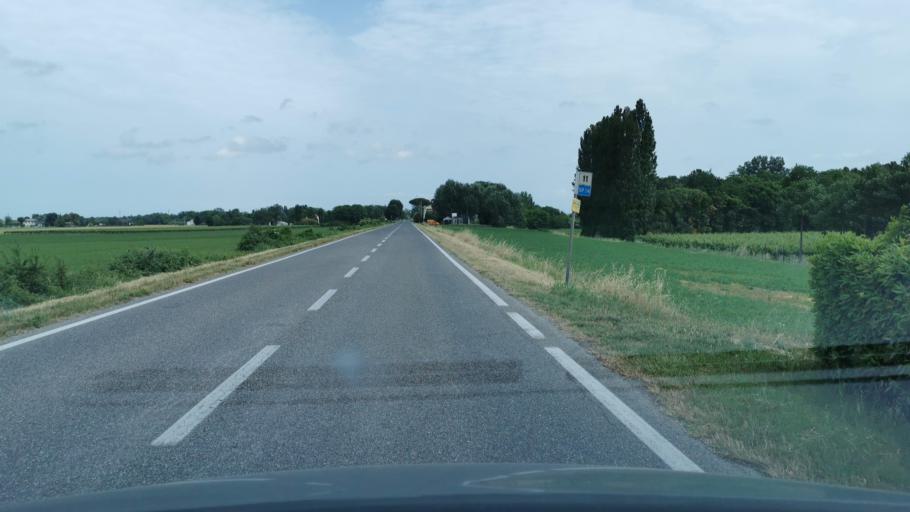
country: IT
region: Emilia-Romagna
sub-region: Provincia di Ravenna
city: Sant'Alberto
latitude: 44.5366
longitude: 12.1669
